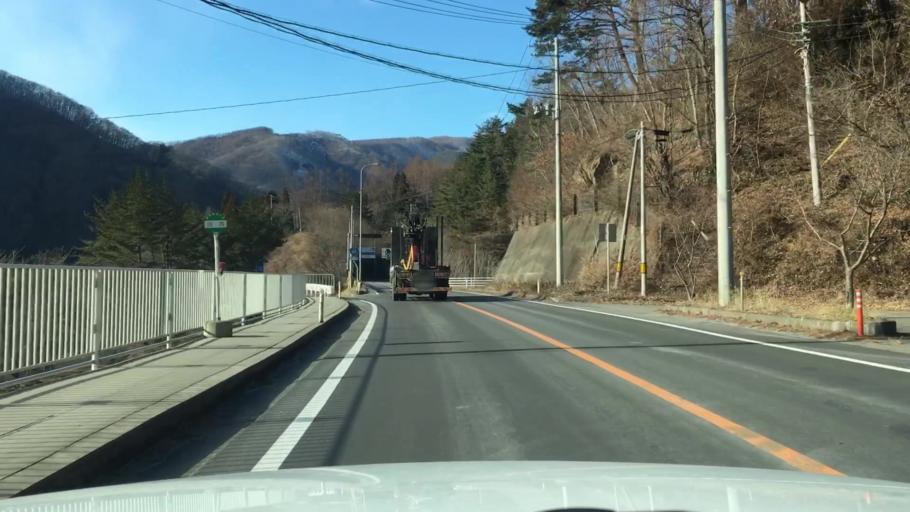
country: JP
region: Iwate
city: Tono
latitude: 39.6414
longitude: 141.5990
